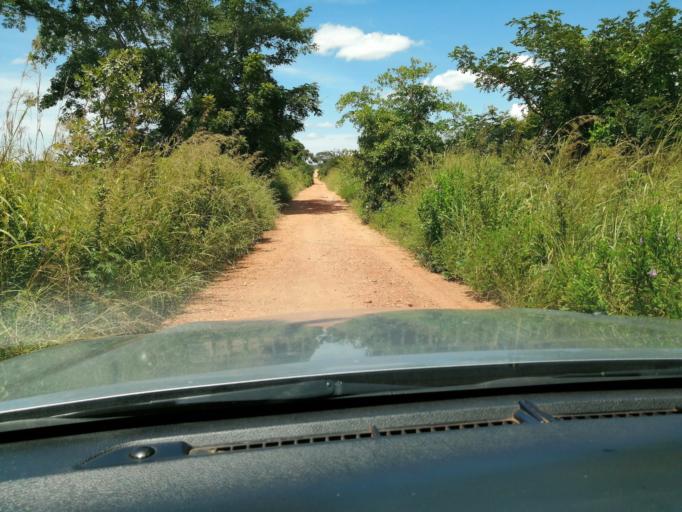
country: ZM
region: Lusaka
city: Lusaka
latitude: -15.1298
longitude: 27.8908
